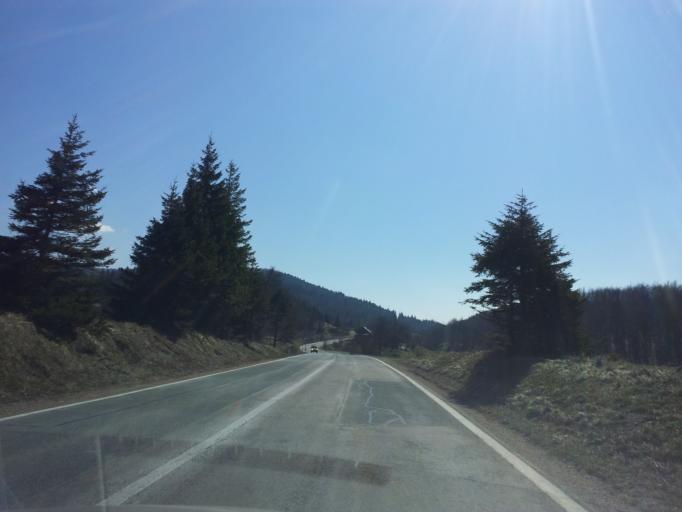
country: HR
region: Licko-Senjska
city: Jezerce
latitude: 44.8101
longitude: 15.6821
